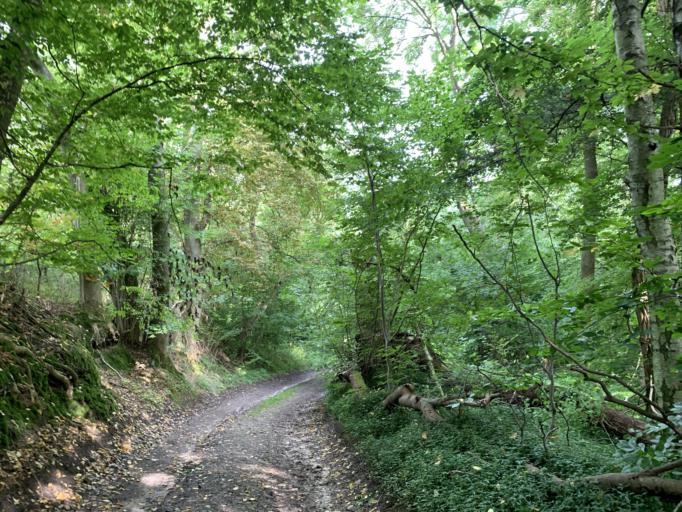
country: DE
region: Mecklenburg-Vorpommern
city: Gross Nemerow
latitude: 53.4248
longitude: 13.1888
